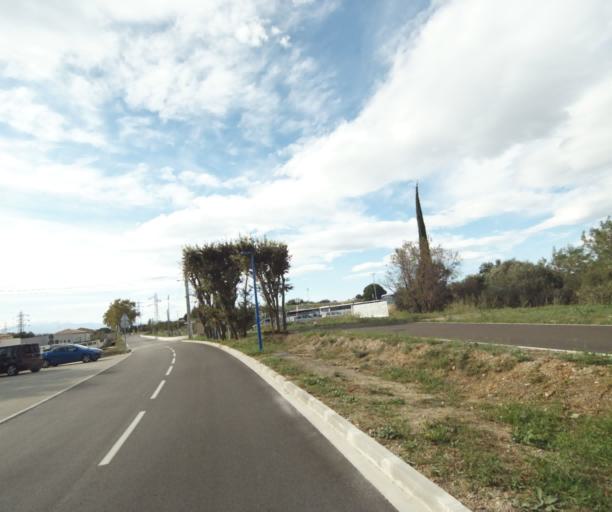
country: FR
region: Languedoc-Roussillon
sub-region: Departement des Pyrenees-Orientales
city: Argelers
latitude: 42.5502
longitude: 3.0102
